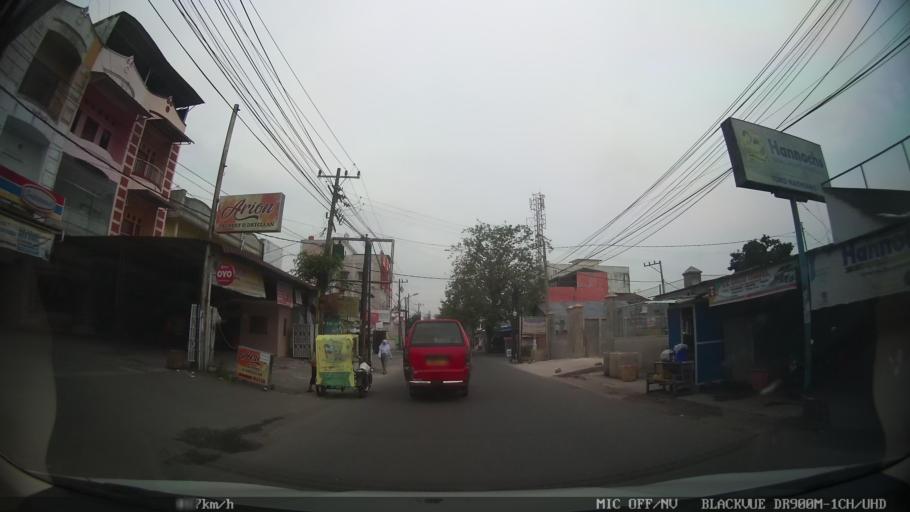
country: ID
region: North Sumatra
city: Medan
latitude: 3.5529
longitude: 98.6956
